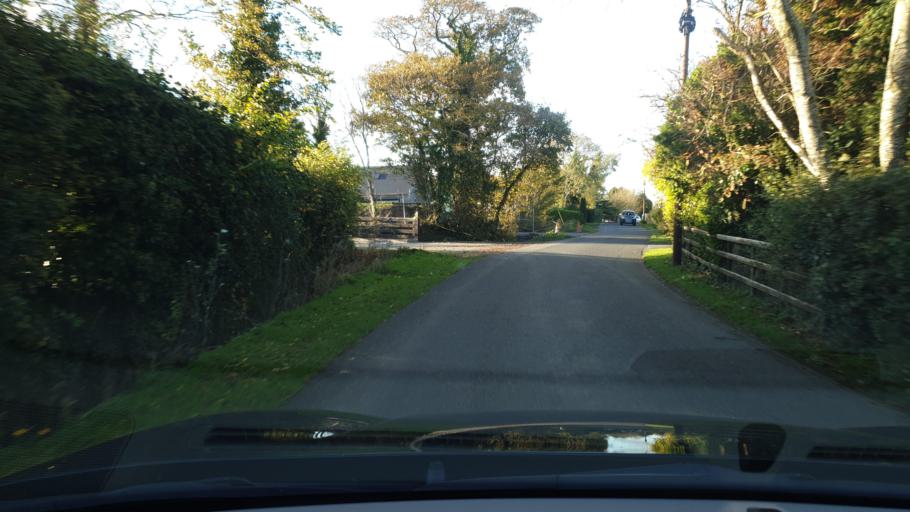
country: IE
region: Leinster
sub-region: An Mhi
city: Stamullin
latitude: 53.6403
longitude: -6.2940
